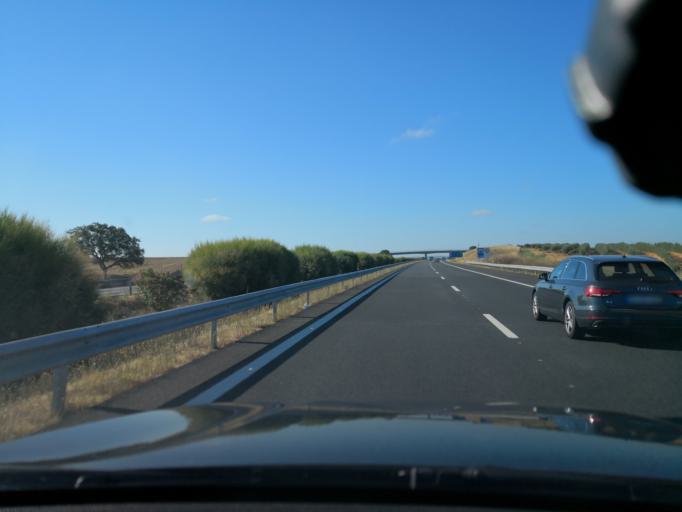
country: PT
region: Beja
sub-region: Aljustrel
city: Aljustrel
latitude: 37.9440
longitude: -8.2459
